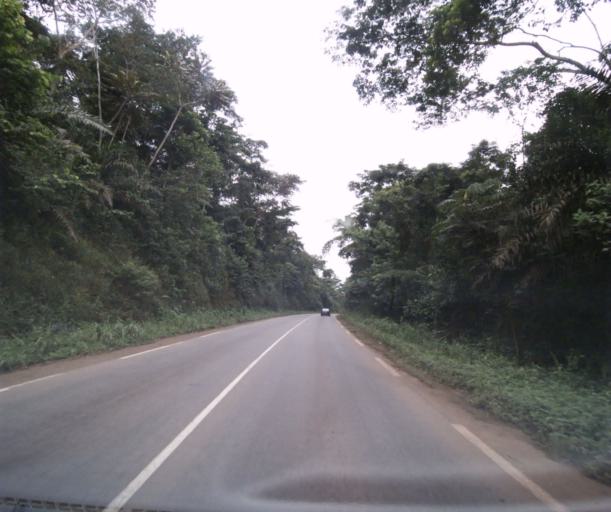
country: CM
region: Centre
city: Mbankomo
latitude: 3.7827
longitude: 11.2801
